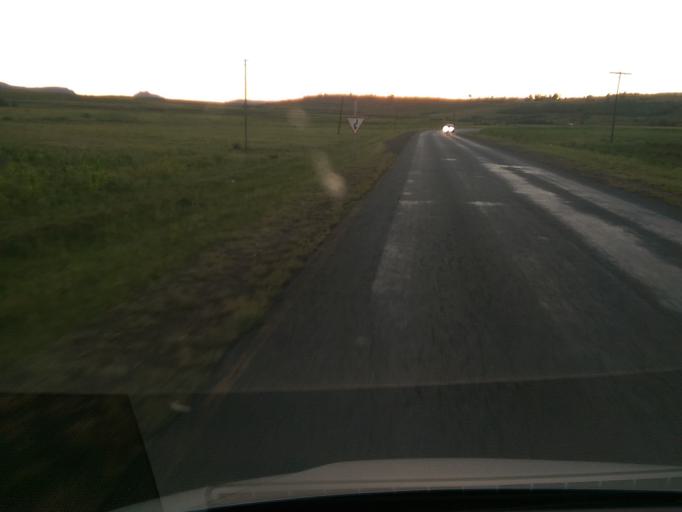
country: LS
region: Maseru
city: Nako
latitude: -29.4377
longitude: 27.6955
